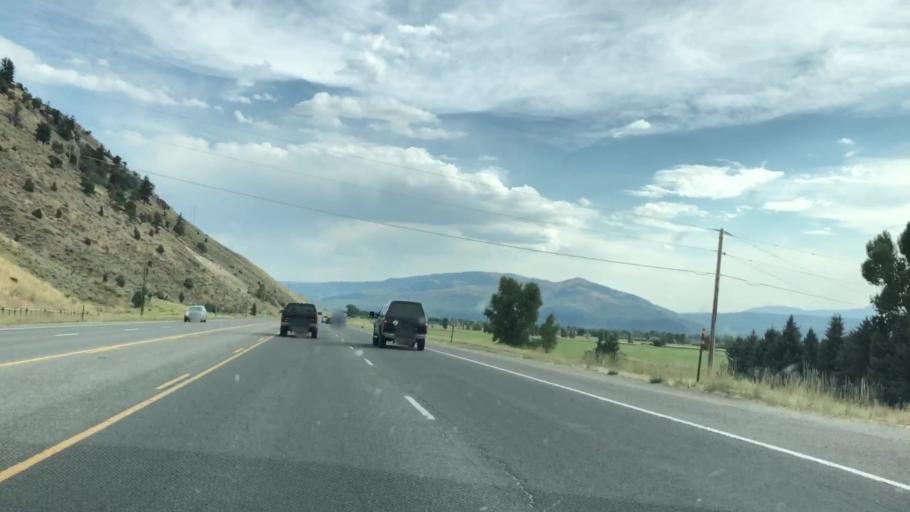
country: US
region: Wyoming
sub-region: Teton County
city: Rafter J Ranch
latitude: 43.4517
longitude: -110.7920
